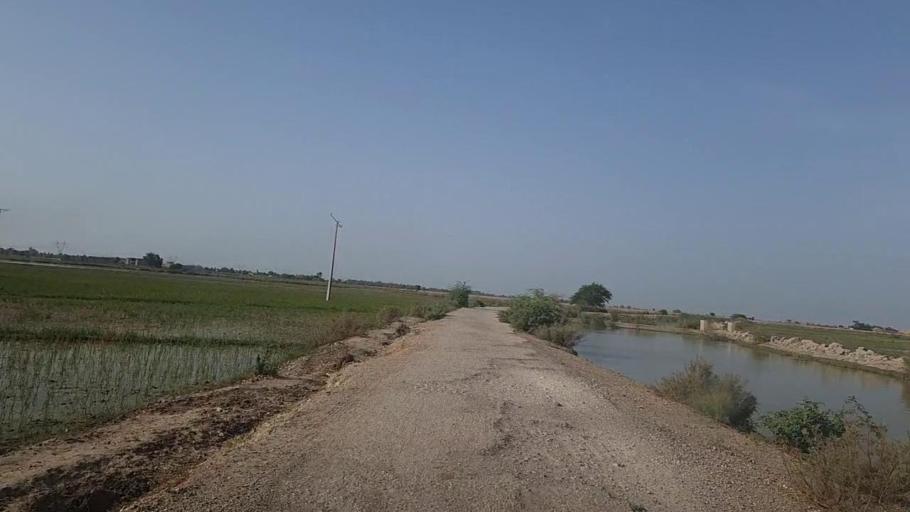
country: PK
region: Sindh
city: Sita Road
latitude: 27.1132
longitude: 67.8774
